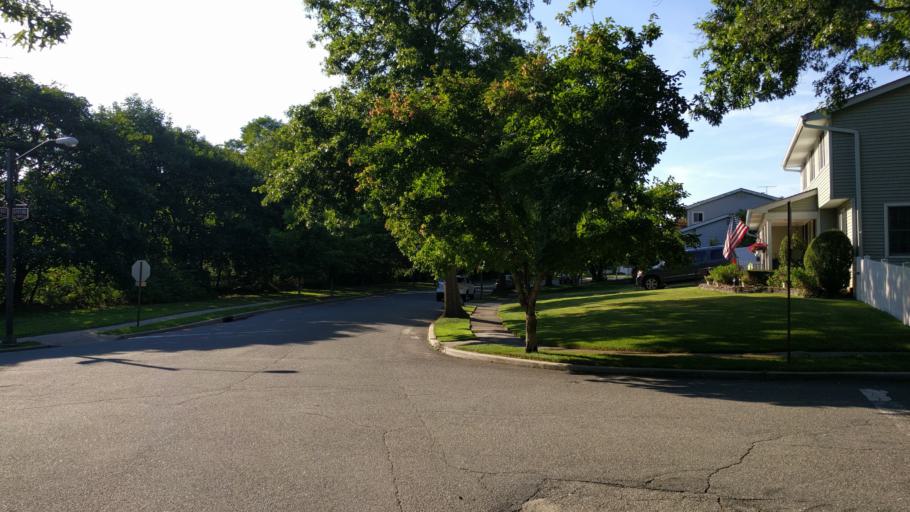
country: US
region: New York
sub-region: Nassau County
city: East Norwich
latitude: 40.8516
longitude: -73.5331
